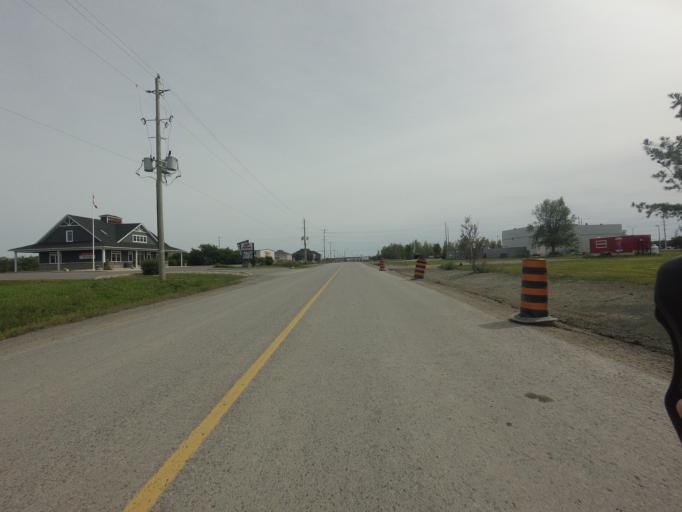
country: CA
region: Ontario
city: Carleton Place
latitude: 45.1413
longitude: -76.1266
